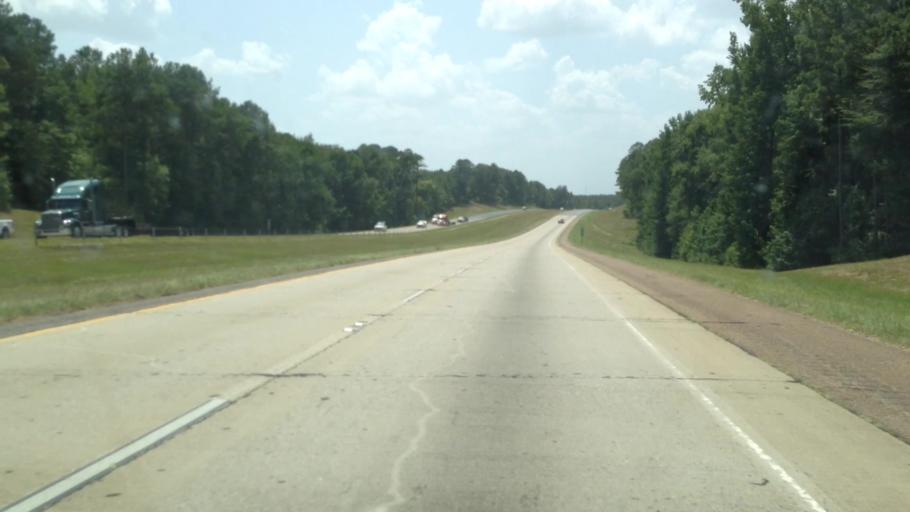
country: US
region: Louisiana
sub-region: Ouachita Parish
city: Claiborne
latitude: 32.5220
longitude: -92.4110
